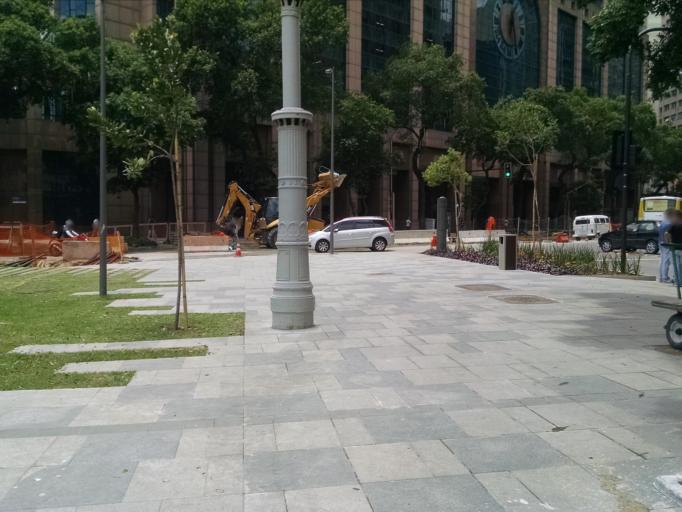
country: BR
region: Rio de Janeiro
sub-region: Rio De Janeiro
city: Rio de Janeiro
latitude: -22.8969
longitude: -43.1810
